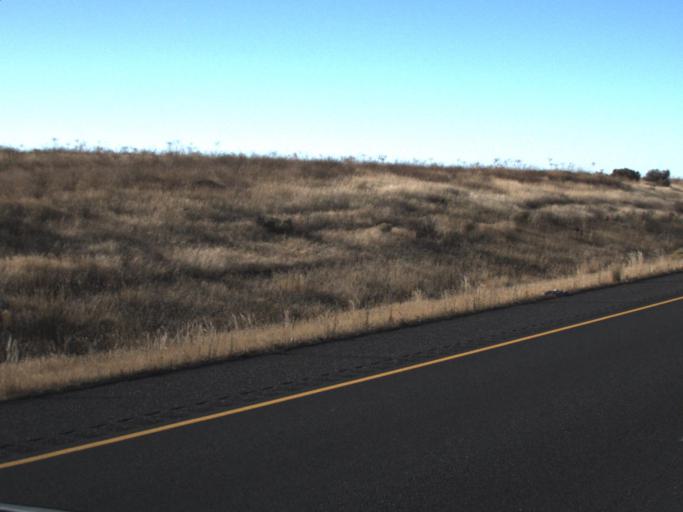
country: US
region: Washington
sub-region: Franklin County
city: Connell
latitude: 46.5917
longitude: -118.9607
